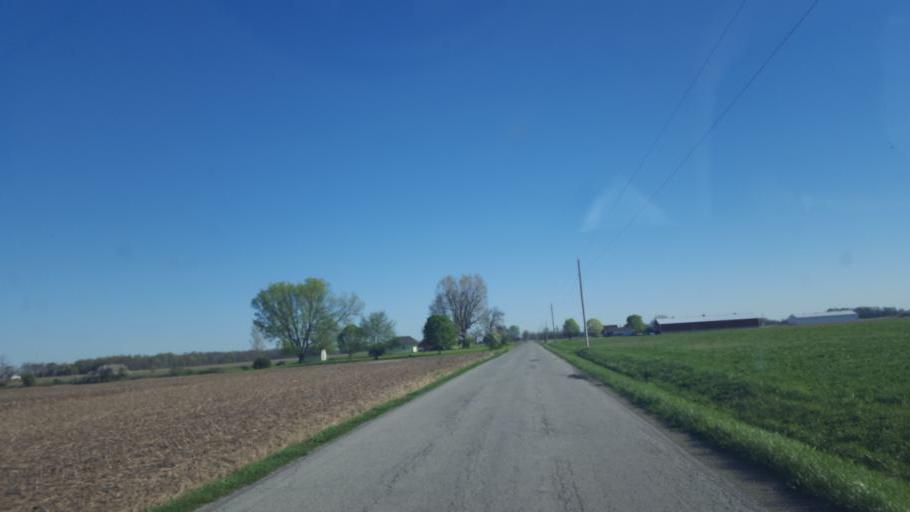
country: US
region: Ohio
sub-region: Morrow County
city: Cardington
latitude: 40.5916
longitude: -82.9186
